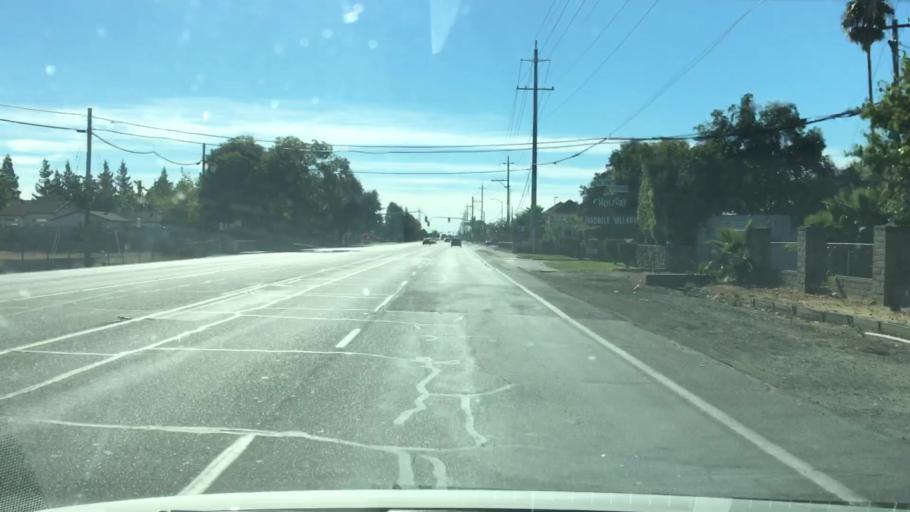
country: US
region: California
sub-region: Sacramento County
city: Florin
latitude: 38.4807
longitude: -121.4220
